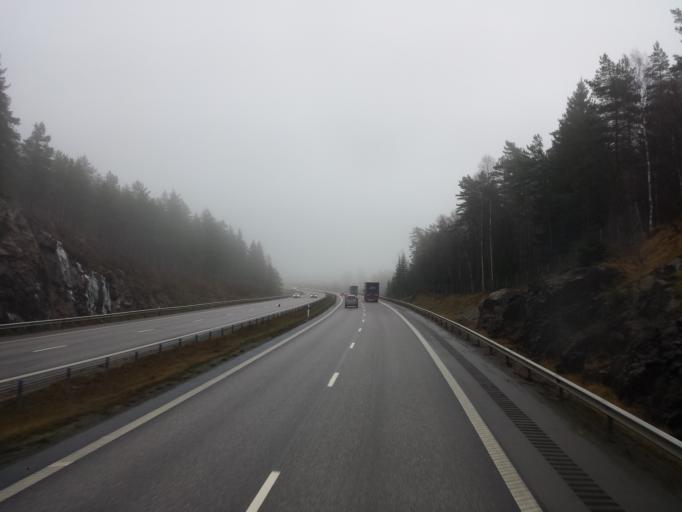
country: SE
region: OEstergoetland
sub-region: Norrkopings Kommun
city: Krokek
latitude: 58.7069
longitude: 16.3543
